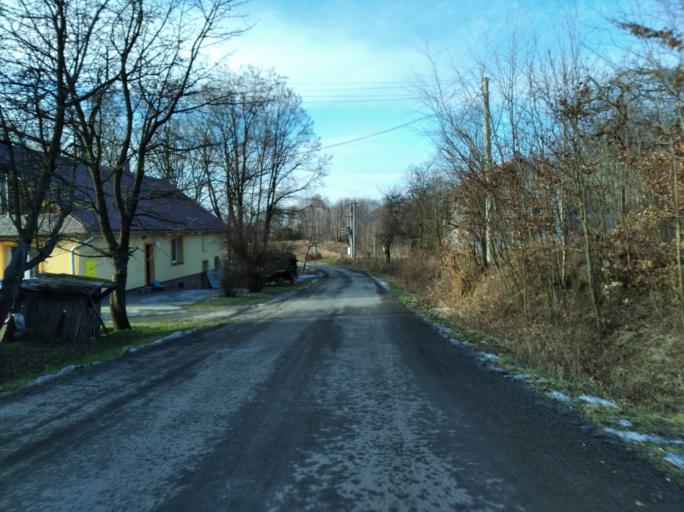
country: PL
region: Subcarpathian Voivodeship
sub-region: Powiat strzyzowski
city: Gwoznica Gorna
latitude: 49.8253
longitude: 21.9800
